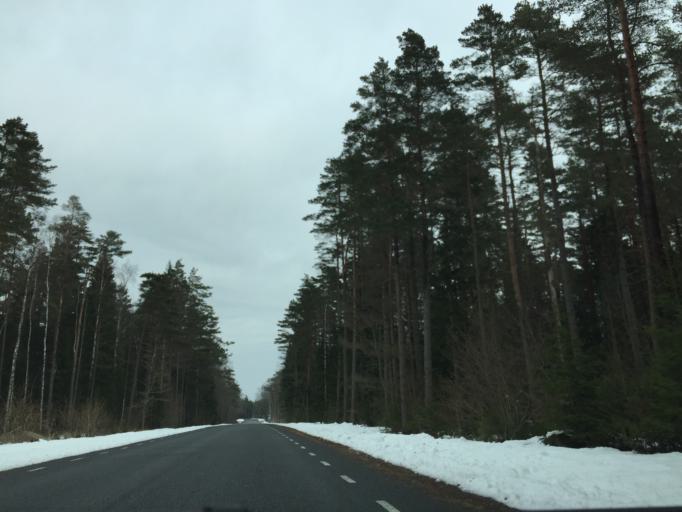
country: EE
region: Saare
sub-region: Kuressaare linn
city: Kuressaare
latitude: 58.4438
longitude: 22.2379
